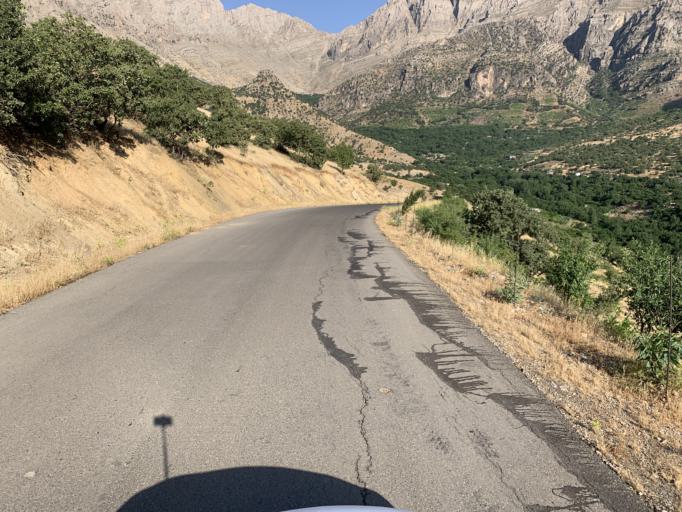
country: IQ
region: As Sulaymaniyah
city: Qeladize
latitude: 35.9955
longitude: 45.1920
